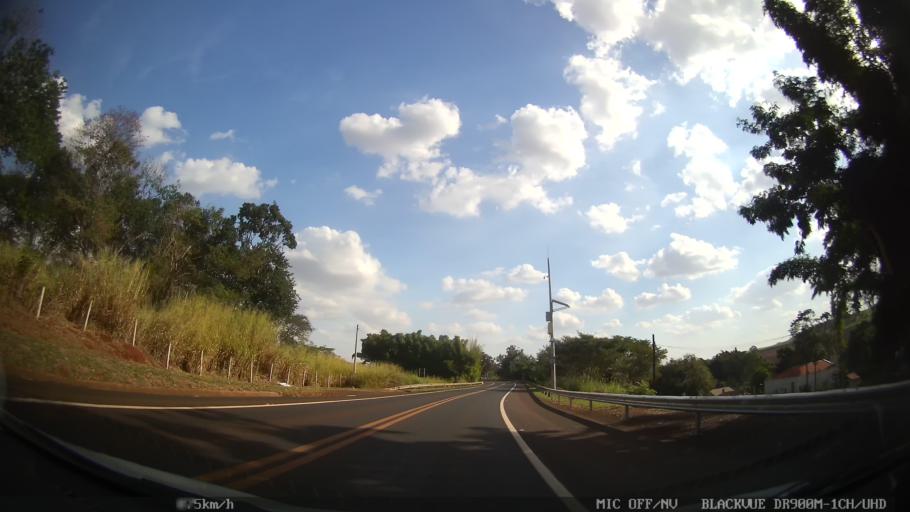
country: BR
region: Sao Paulo
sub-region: Ribeirao Preto
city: Ribeirao Preto
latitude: -21.1957
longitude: -47.8731
